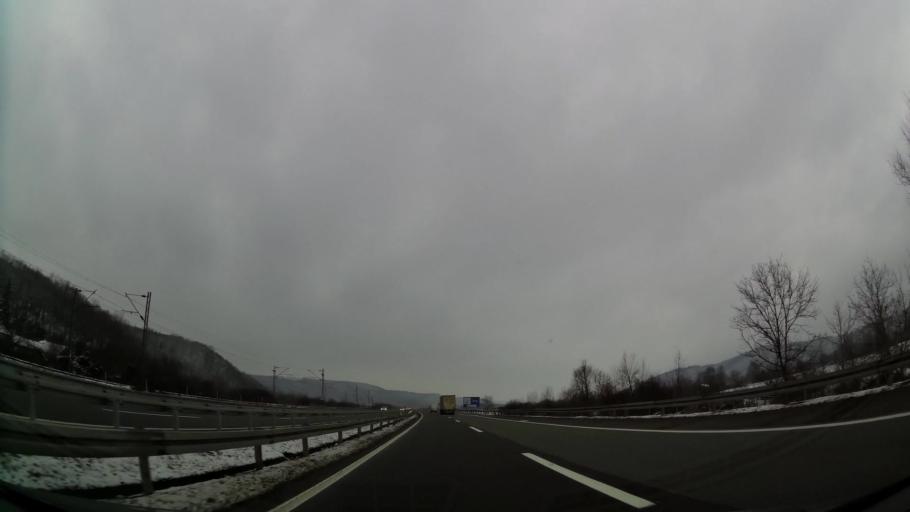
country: RS
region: Central Serbia
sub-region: Pomoravski Okrug
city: Jagodina
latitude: 44.0532
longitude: 21.2314
